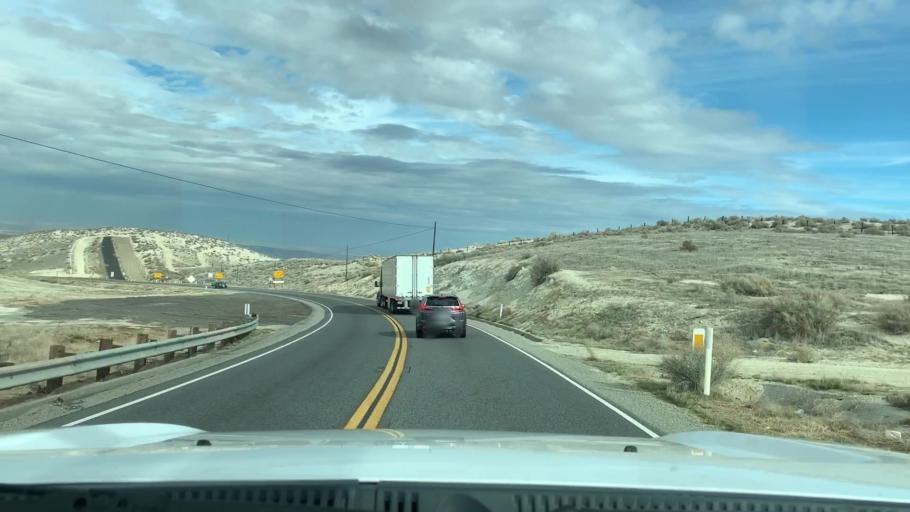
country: US
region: California
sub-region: Kern County
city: Maricopa
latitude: 34.9966
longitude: -119.4200
